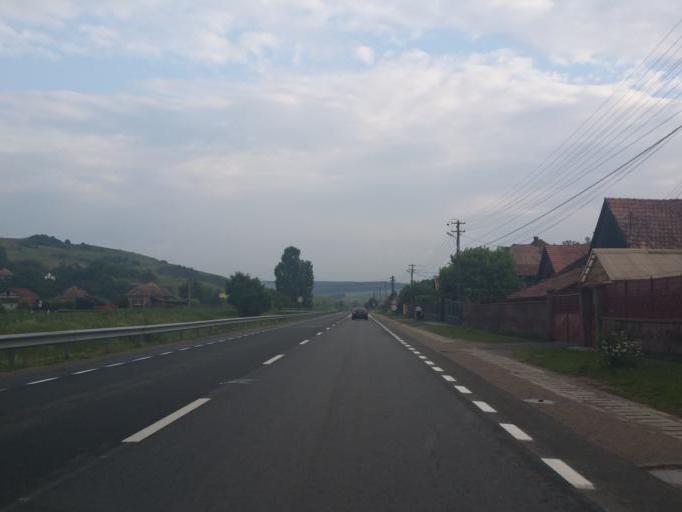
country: RO
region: Cluj
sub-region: Comuna Sanpaul
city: Sanpaul
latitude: 46.8694
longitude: 23.4134
